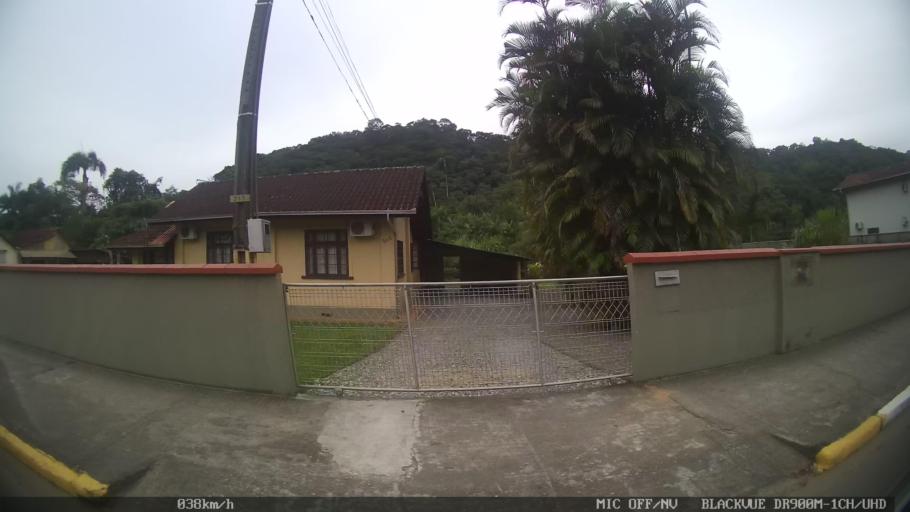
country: BR
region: Santa Catarina
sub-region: Joinville
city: Joinville
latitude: -26.2129
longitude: -48.9108
